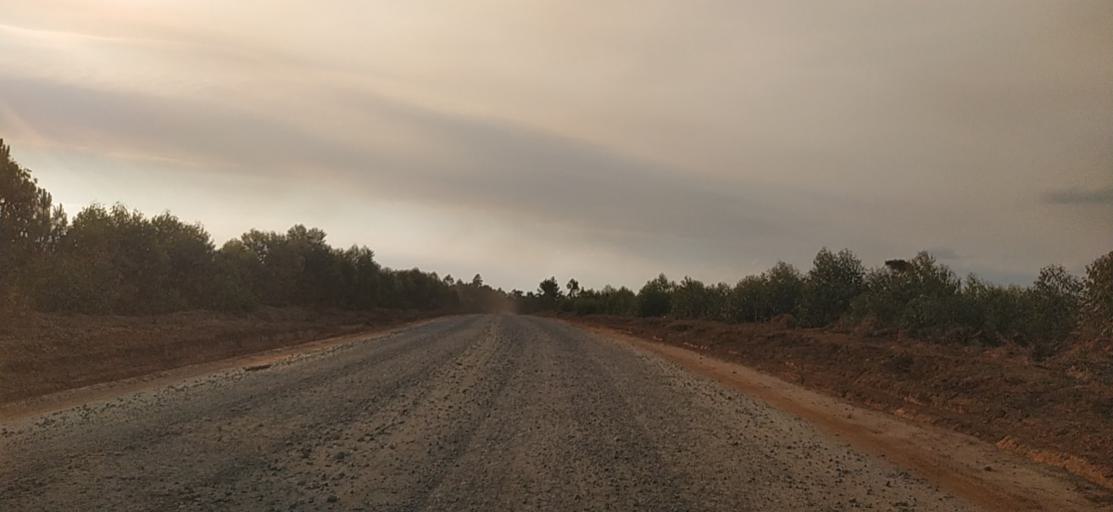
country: MG
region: Alaotra Mangoro
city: Moramanga
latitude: -18.5632
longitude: 48.2634
